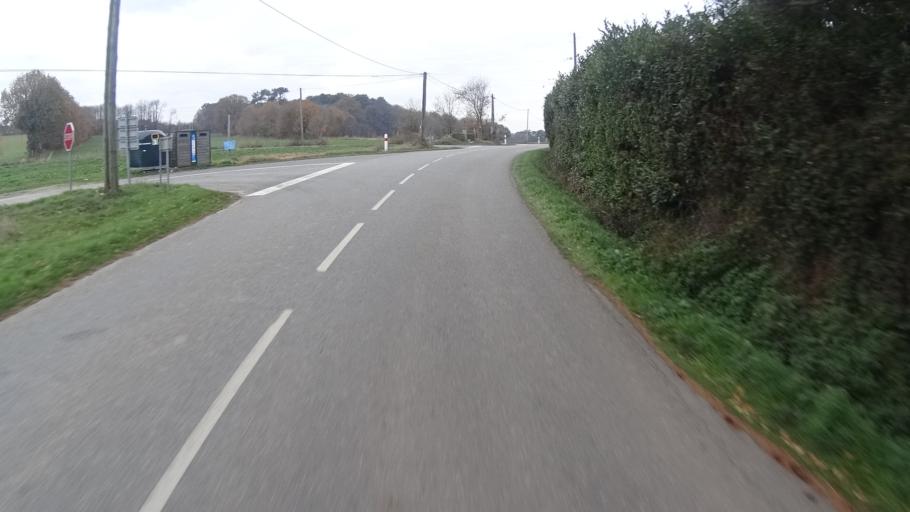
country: FR
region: Pays de la Loire
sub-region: Departement de la Loire-Atlantique
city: Avessac
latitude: 47.6543
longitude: -1.9575
